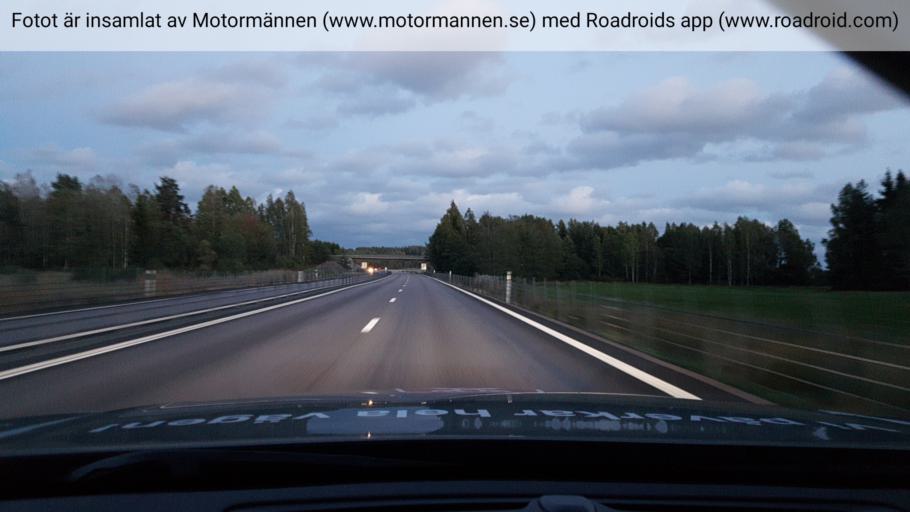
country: SE
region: Vaermland
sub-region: Karlstads Kommun
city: Skattkarr
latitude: 59.4058
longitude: 13.7717
